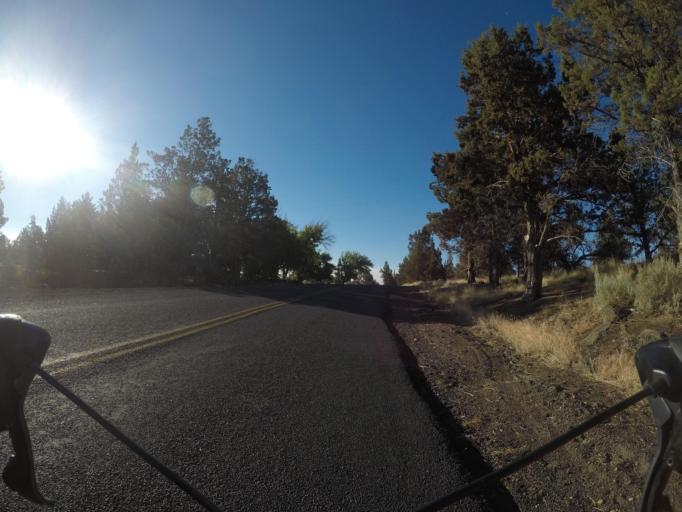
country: US
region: Oregon
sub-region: Deschutes County
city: Redmond
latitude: 44.2669
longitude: -121.2493
